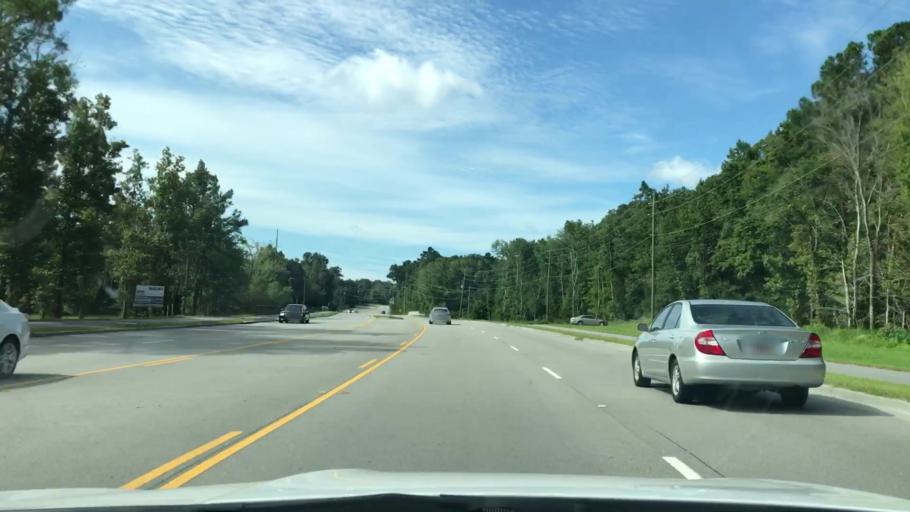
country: US
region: South Carolina
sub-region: Dorchester County
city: Centerville
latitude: 32.9759
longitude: -80.1977
